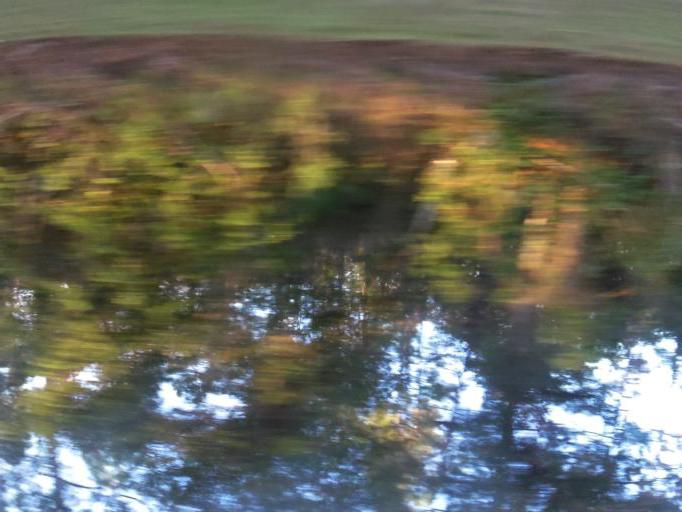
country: US
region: Florida
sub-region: Clay County
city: Green Cove Springs
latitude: 29.9400
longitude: -81.5639
